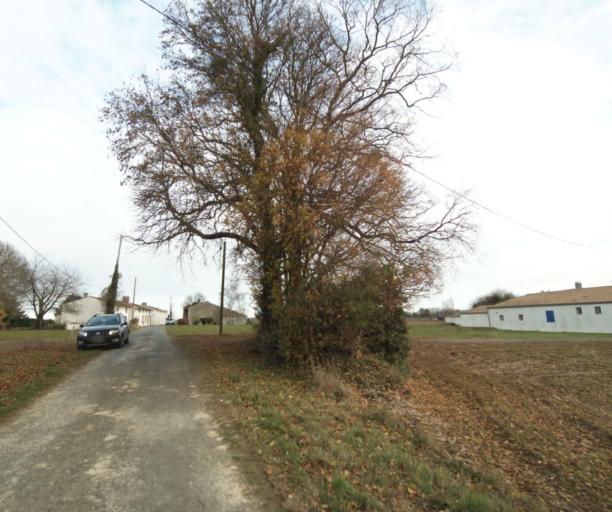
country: FR
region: Poitou-Charentes
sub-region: Departement de la Charente-Maritime
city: Corme-Royal
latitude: 45.7830
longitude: -0.8240
